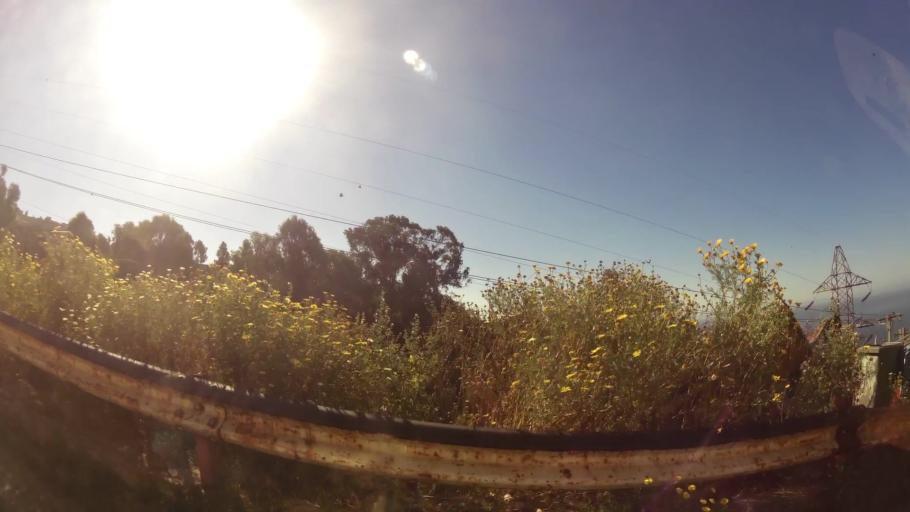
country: CL
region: Valparaiso
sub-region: Provincia de Valparaiso
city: Valparaiso
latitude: -33.0578
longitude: -71.6223
